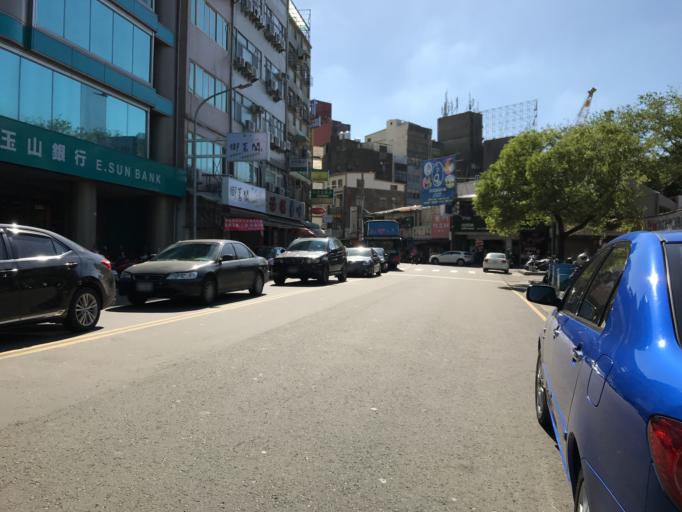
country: TW
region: Taiwan
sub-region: Hsinchu
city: Hsinchu
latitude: 24.8051
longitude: 120.9727
